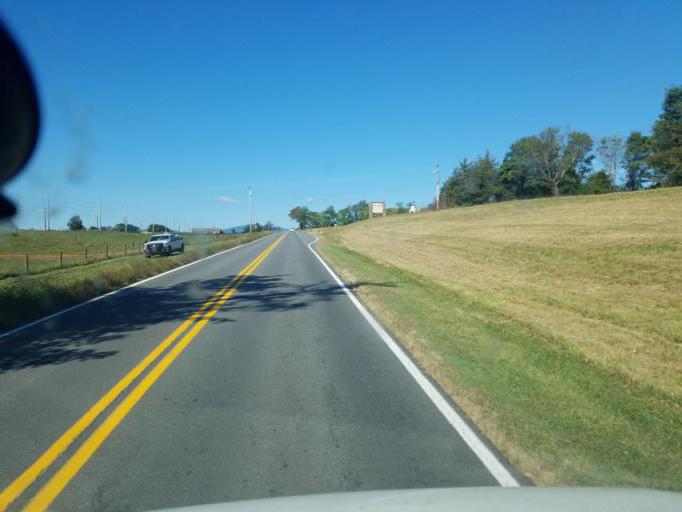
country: US
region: Virginia
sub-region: Madison County
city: Madison
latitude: 38.3477
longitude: -78.2901
